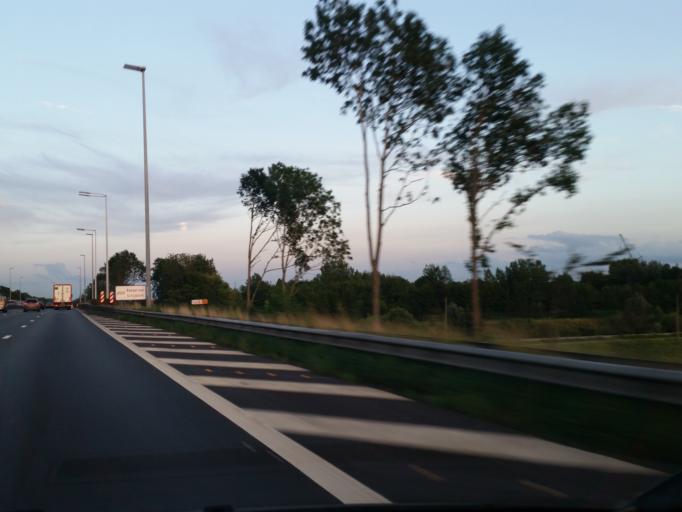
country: BE
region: Flanders
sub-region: Provincie Oost-Vlaanderen
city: Nevele
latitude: 51.0515
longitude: 3.5646
